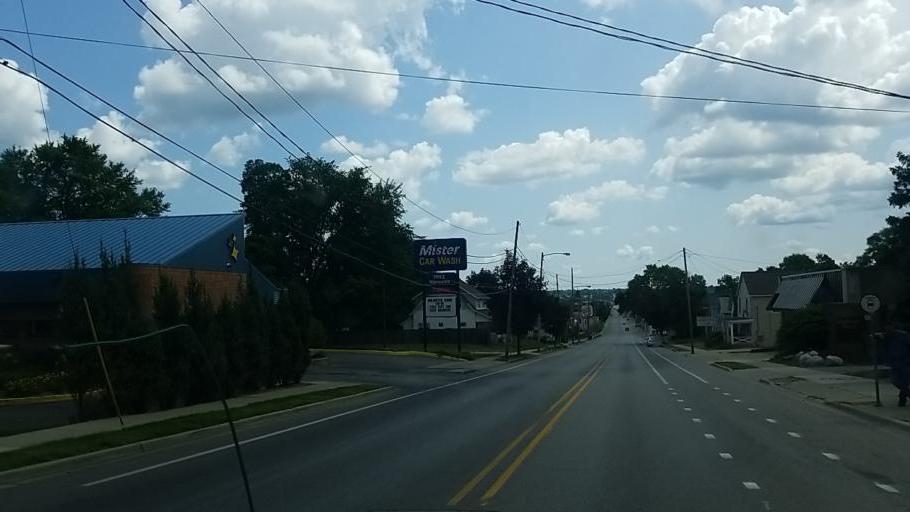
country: US
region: Michigan
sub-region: Kent County
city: Grand Rapids
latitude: 42.9856
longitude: -85.7016
